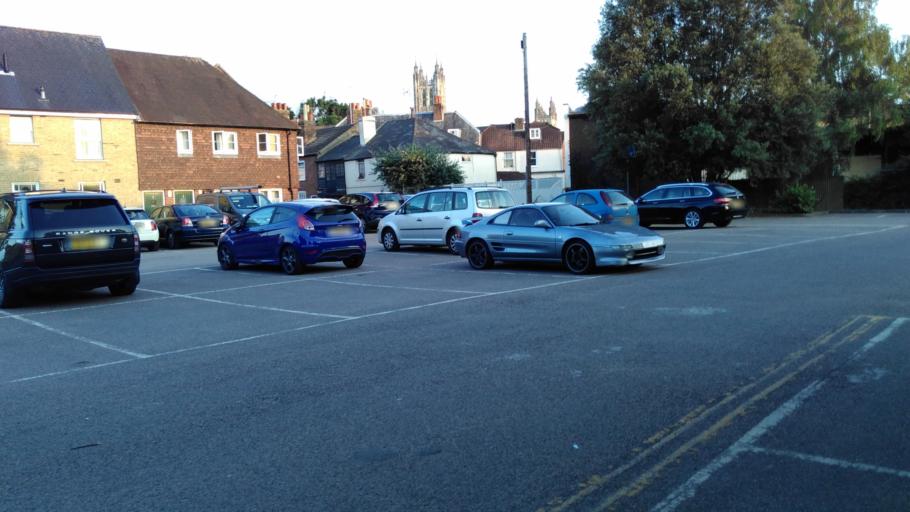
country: GB
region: England
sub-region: Kent
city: Canterbury
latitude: 51.2834
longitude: 1.0821
